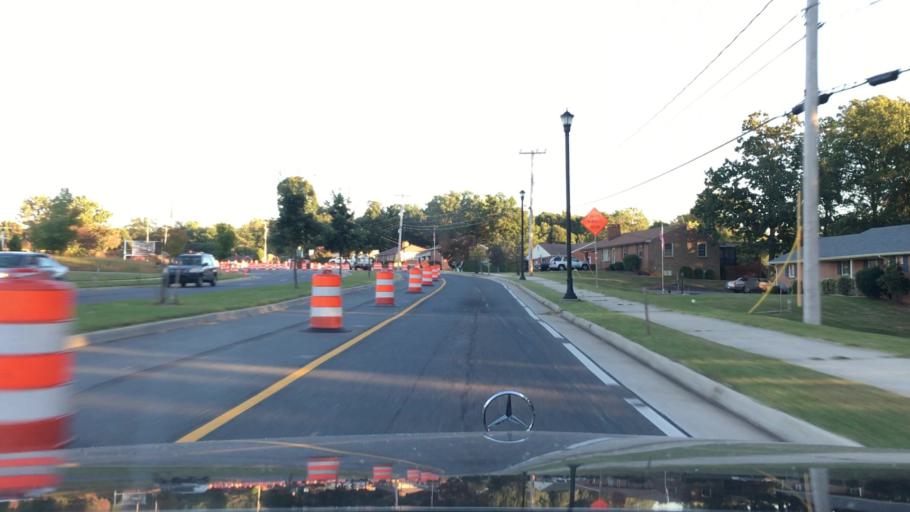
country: US
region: Virginia
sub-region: Campbell County
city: Timberlake
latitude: 37.3373
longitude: -79.2221
